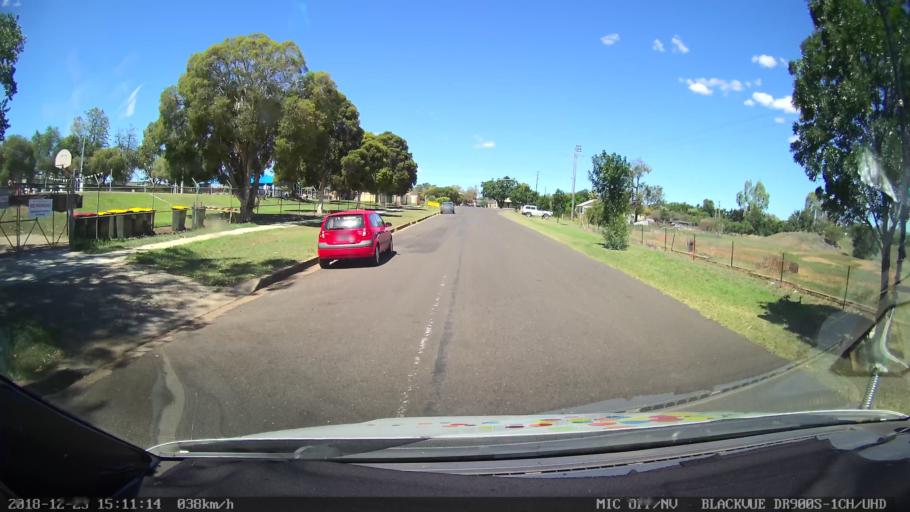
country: AU
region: New South Wales
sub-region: Tamworth Municipality
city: Manilla
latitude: -30.7509
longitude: 150.7244
